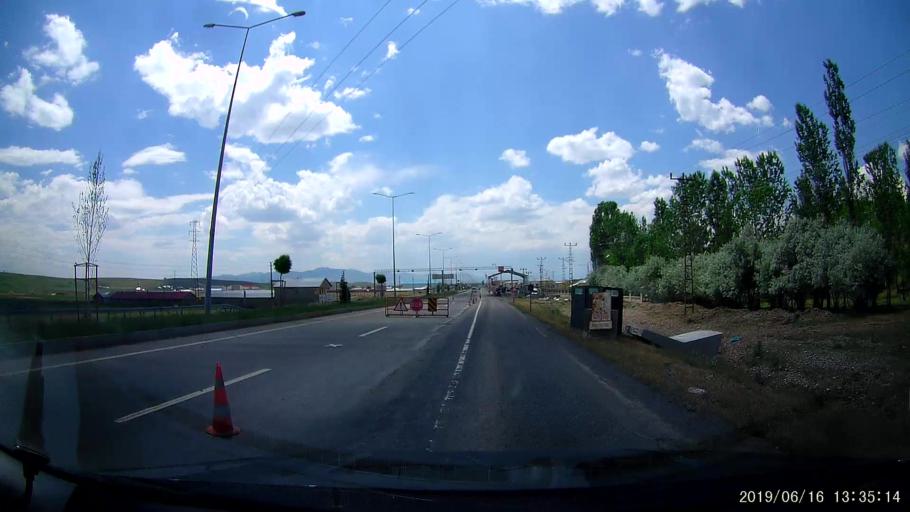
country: TR
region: Agri
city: Agri
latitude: 39.7129
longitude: 43.1118
